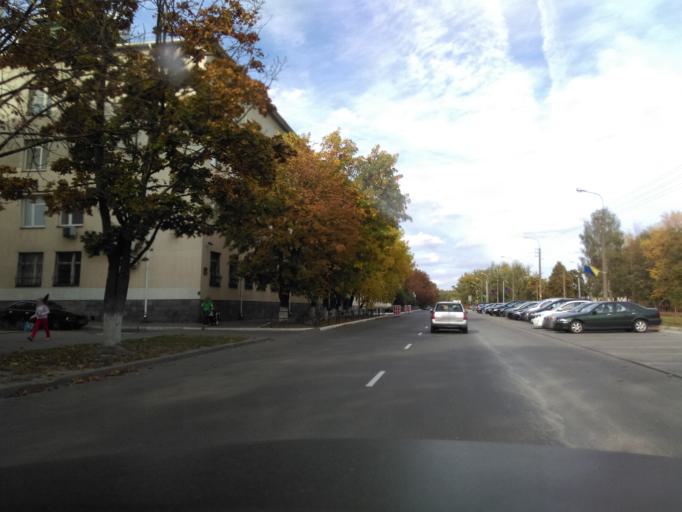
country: BY
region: Minsk
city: Minsk
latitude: 53.9054
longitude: 27.6022
